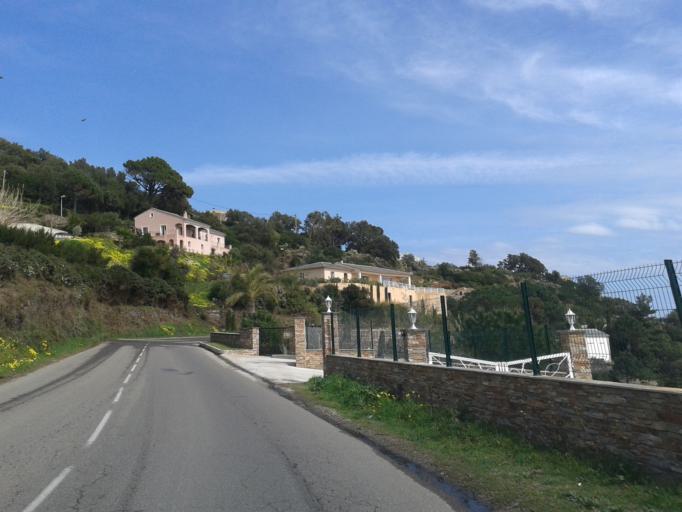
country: FR
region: Corsica
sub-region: Departement de la Haute-Corse
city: Brando
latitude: 42.7805
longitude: 9.4786
